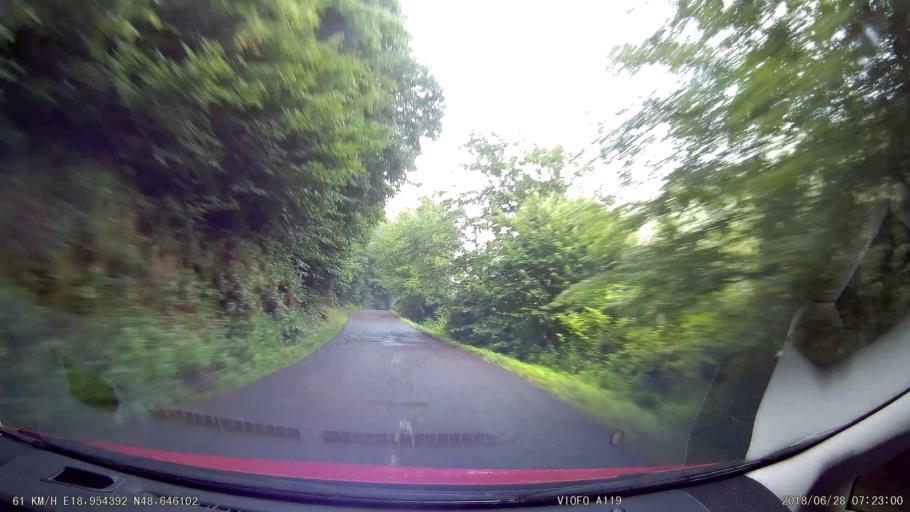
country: SK
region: Banskobystricky
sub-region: Okres Ziar nad Hronom
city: Kremnica
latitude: 48.6459
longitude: 18.9545
